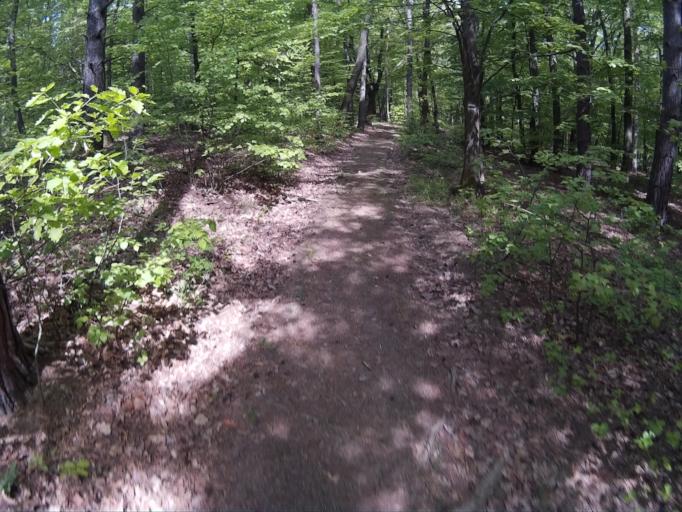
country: HU
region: Vas
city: Koszeg
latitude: 47.3550
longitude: 16.5038
